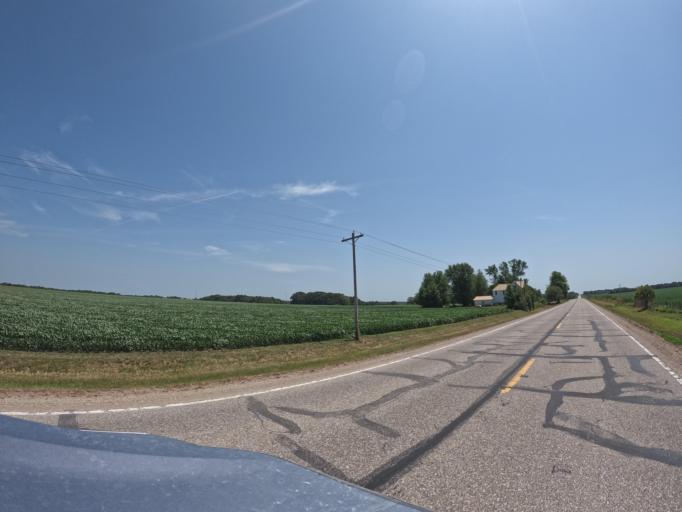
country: US
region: Iowa
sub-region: Henry County
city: Mount Pleasant
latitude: 40.9734
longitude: -91.6124
